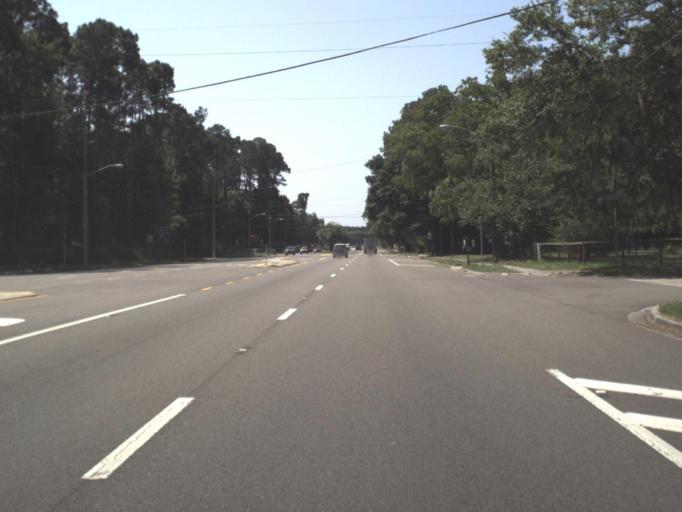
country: US
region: Florida
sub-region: Duval County
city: Jacksonville
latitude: 30.4448
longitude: -81.7016
